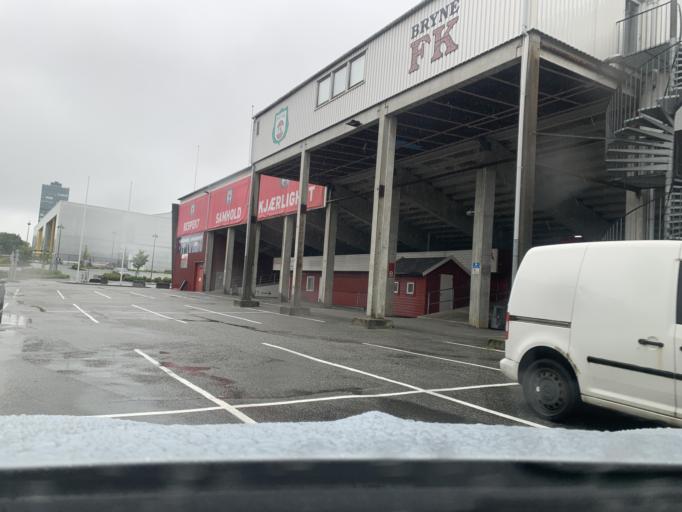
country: NO
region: Rogaland
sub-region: Time
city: Bryne
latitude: 58.7300
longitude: 5.6490
